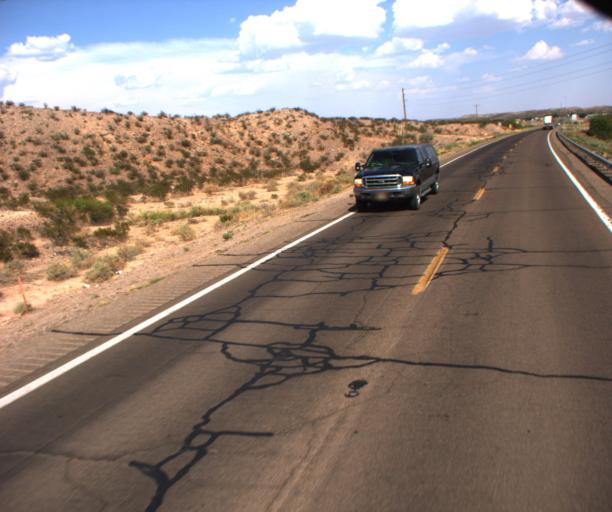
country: US
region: Arizona
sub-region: Greenlee County
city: Clifton
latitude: 32.7481
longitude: -109.1084
